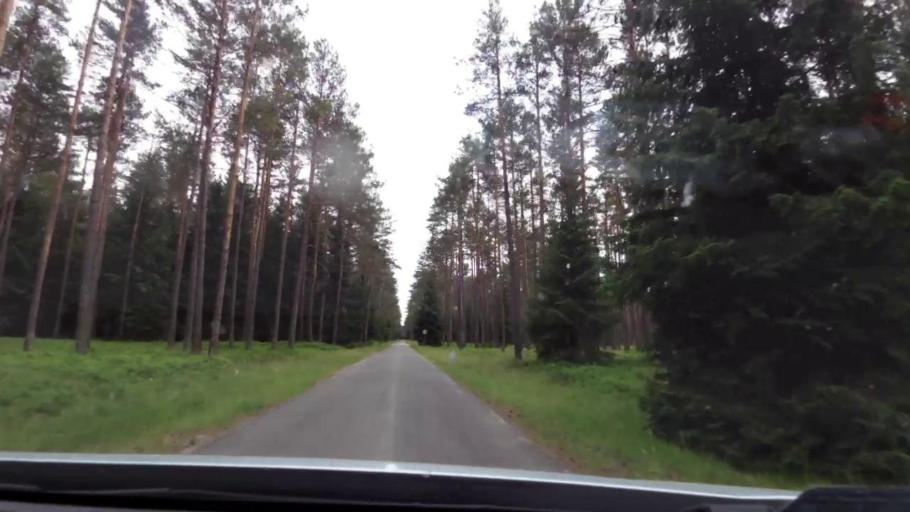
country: PL
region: Pomeranian Voivodeship
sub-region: Powiat bytowski
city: Trzebielino
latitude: 54.2168
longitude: 17.0035
